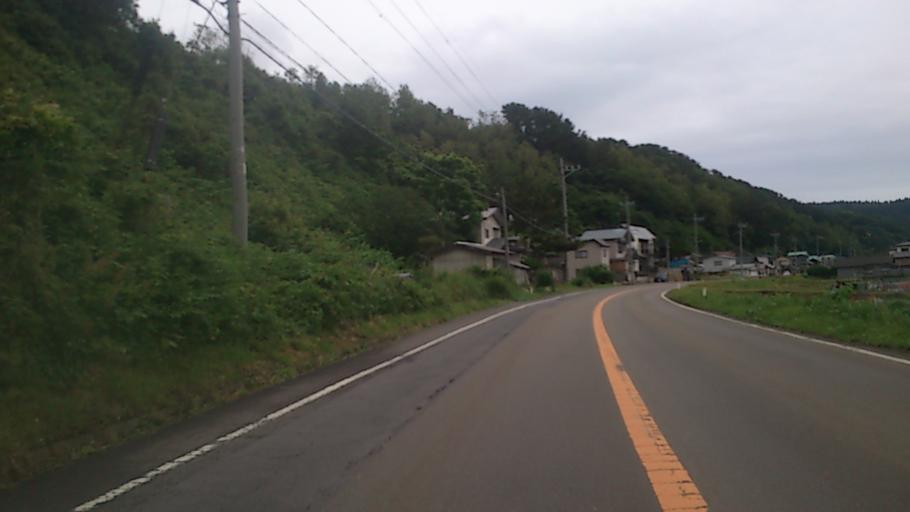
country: JP
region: Akita
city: Noshiromachi
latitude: 40.4972
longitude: 139.9511
